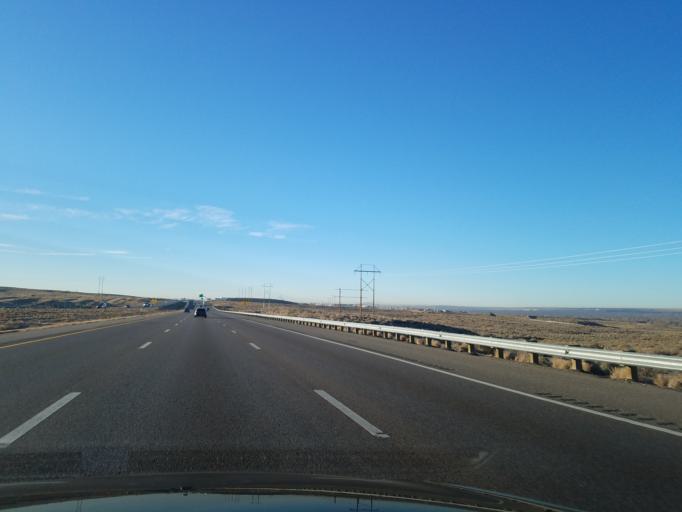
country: US
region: New Mexico
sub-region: Sandoval County
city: Corrales
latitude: 35.2215
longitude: -106.5733
